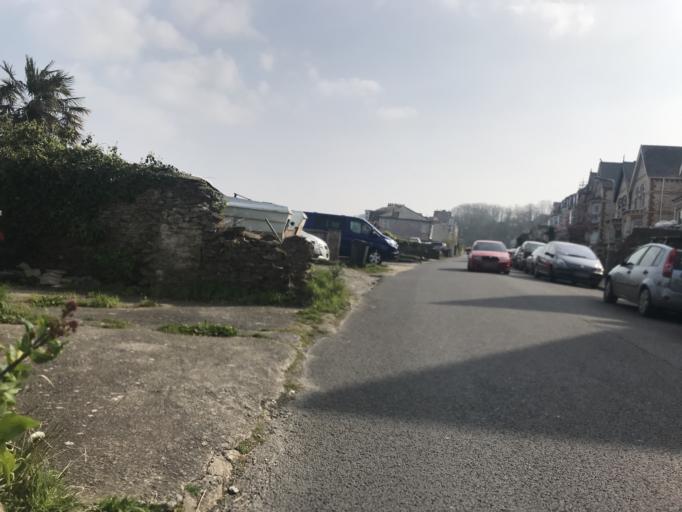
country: GB
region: England
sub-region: Devon
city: Ilfracombe
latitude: 51.2039
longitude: -4.1271
